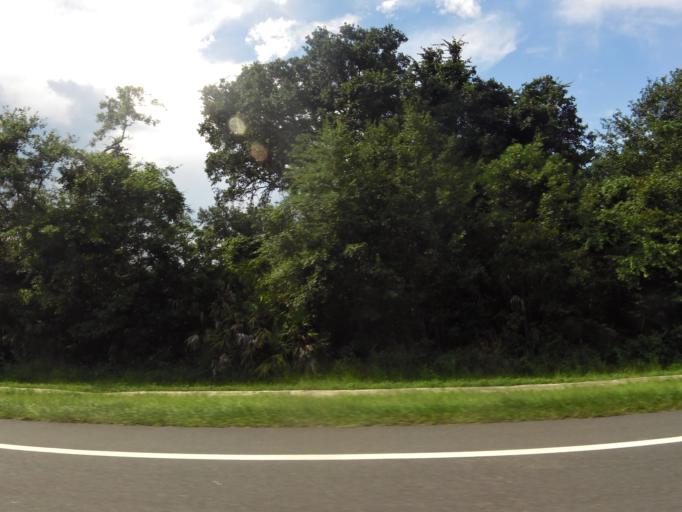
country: US
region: Florida
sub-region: Nassau County
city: Fernandina Beach
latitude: 30.6041
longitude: -81.4565
